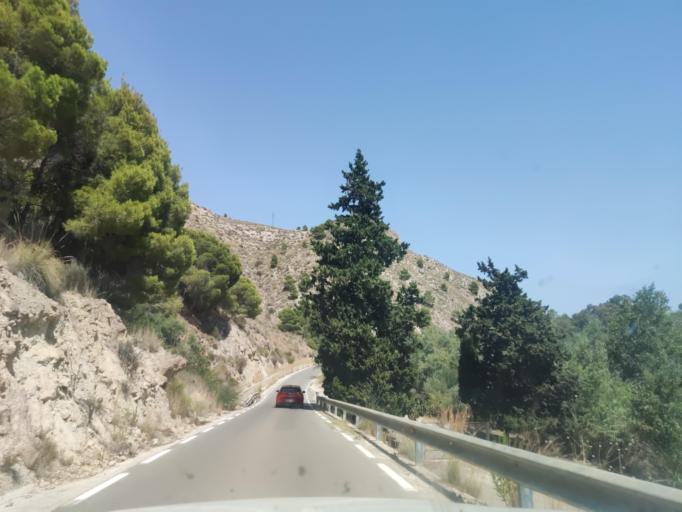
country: ES
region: Murcia
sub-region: Murcia
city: Archena
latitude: 38.1308
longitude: -1.3072
